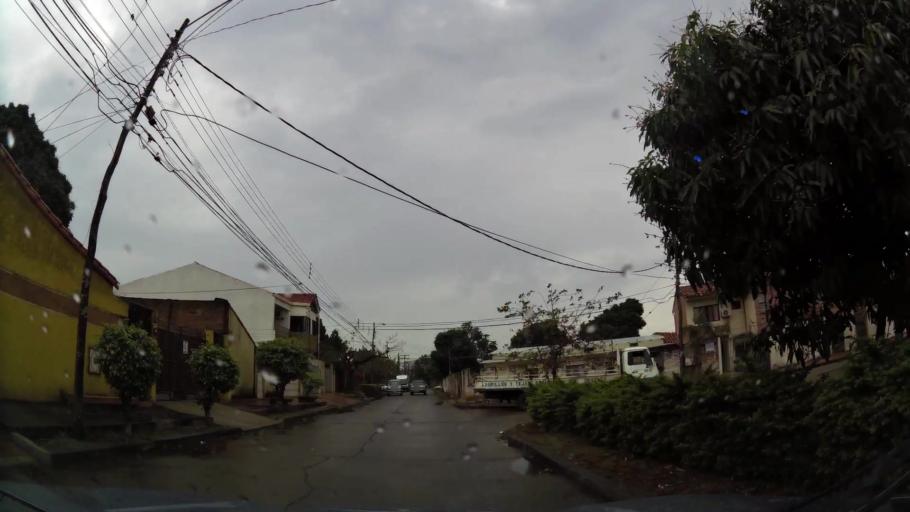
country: BO
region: Santa Cruz
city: Santa Cruz de la Sierra
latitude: -17.7697
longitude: -63.1500
